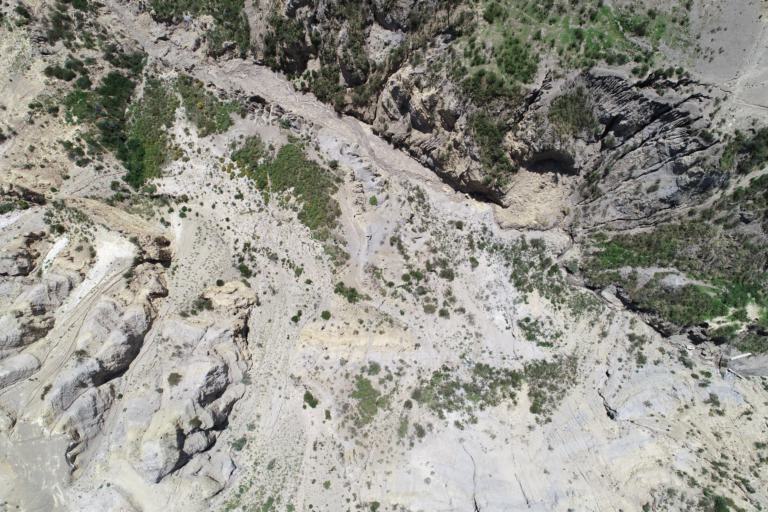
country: BO
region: La Paz
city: La Paz
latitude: -16.5209
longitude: -68.0491
